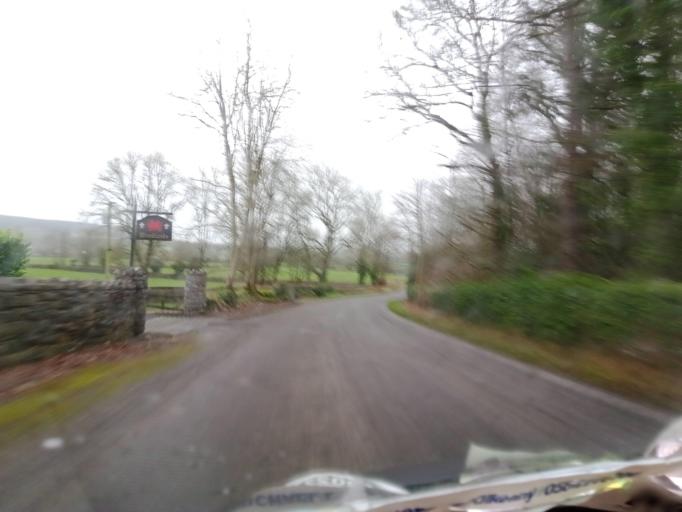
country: IE
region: Munster
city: Fethard
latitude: 52.5555
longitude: -7.7638
